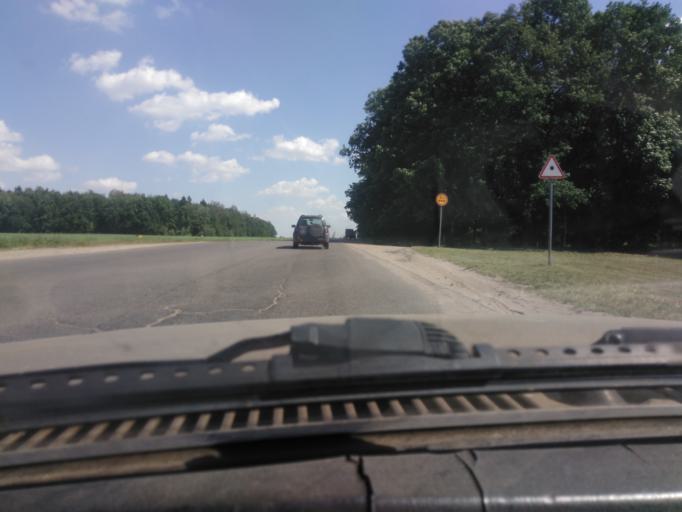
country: BY
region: Mogilev
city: Palykavichy Pyershyya
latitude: 53.9558
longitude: 30.3642
